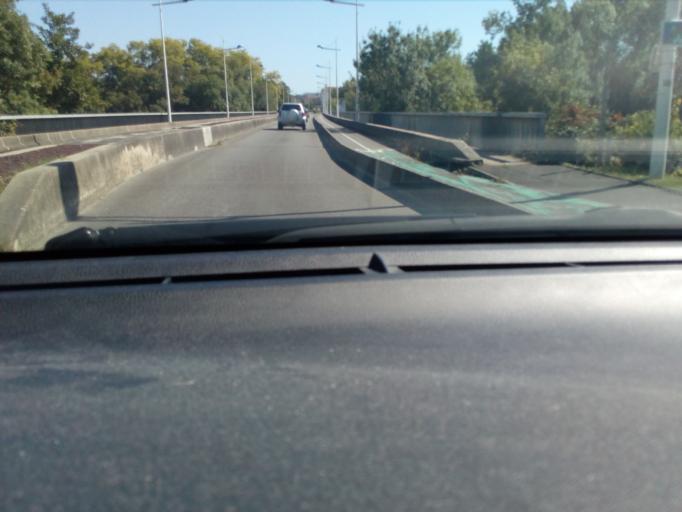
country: FR
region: Poitou-Charentes
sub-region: Departement de la Charente
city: Angouleme
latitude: 45.6624
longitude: 0.1570
